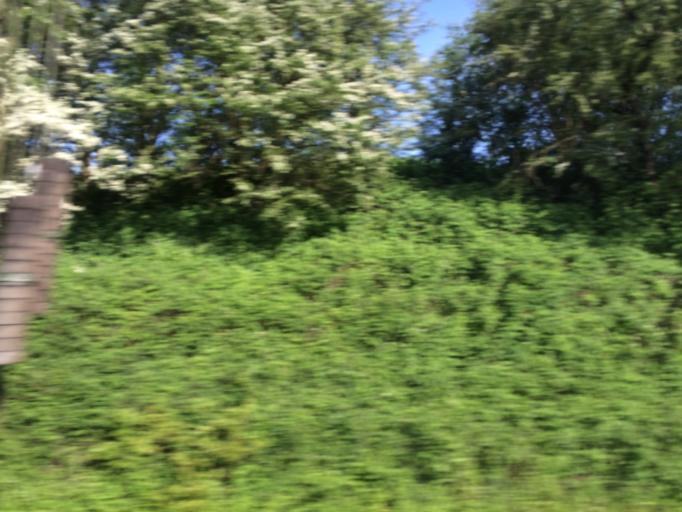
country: DE
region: North Rhine-Westphalia
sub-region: Regierungsbezirk Koln
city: Bonn
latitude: 50.7522
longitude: 7.1331
